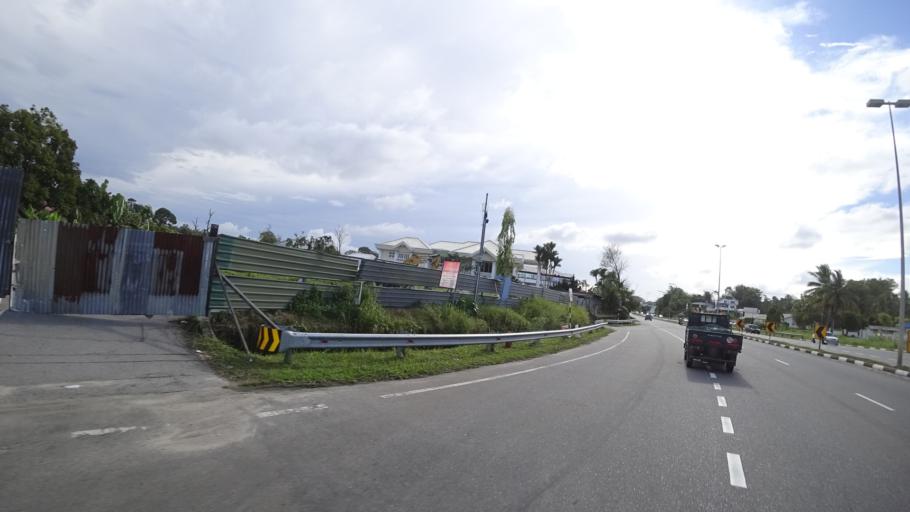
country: BN
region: Brunei and Muara
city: Bandar Seri Begawan
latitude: 4.8796
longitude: 114.8715
